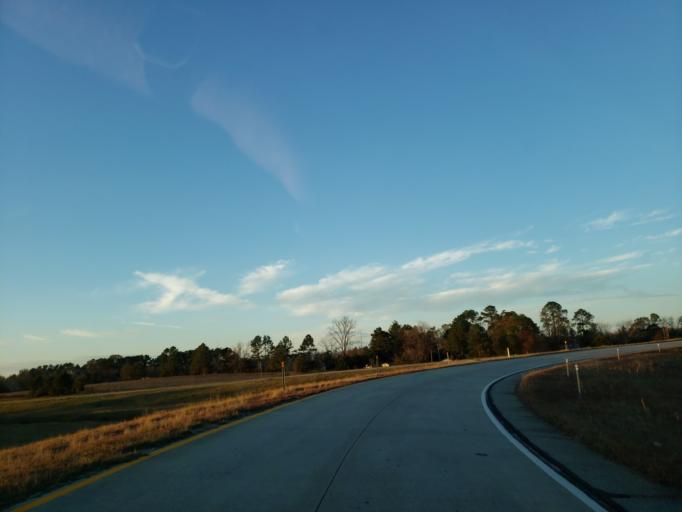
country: US
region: Georgia
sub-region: Crisp County
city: Cordele
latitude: 31.9219
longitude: -83.7731
